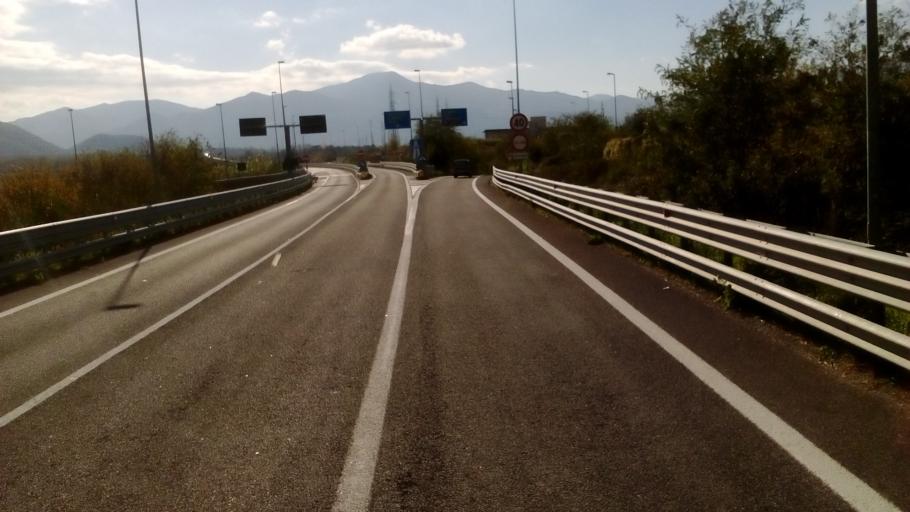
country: IT
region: Molise
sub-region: Provincia di Isernia
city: Taverna Ravindola
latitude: 41.5102
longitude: 14.1145
